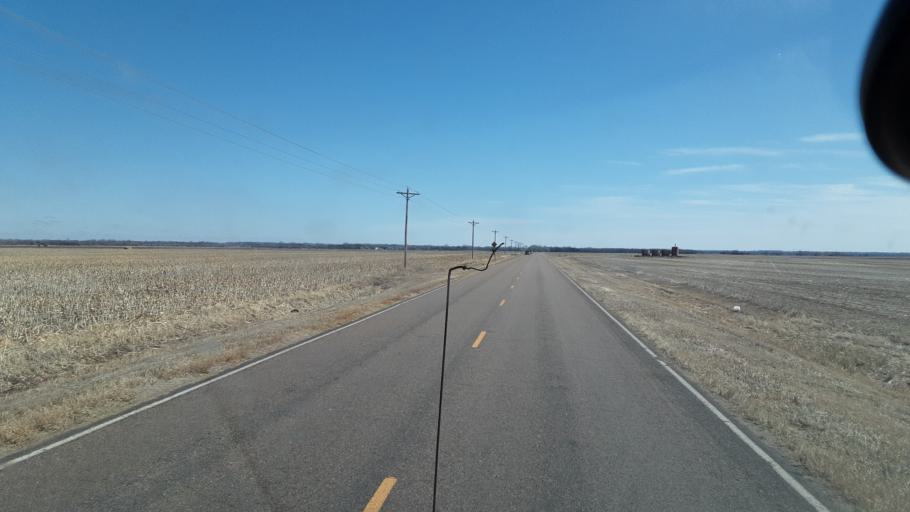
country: US
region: Kansas
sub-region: Reno County
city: Nickerson
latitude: 38.2177
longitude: -98.1010
